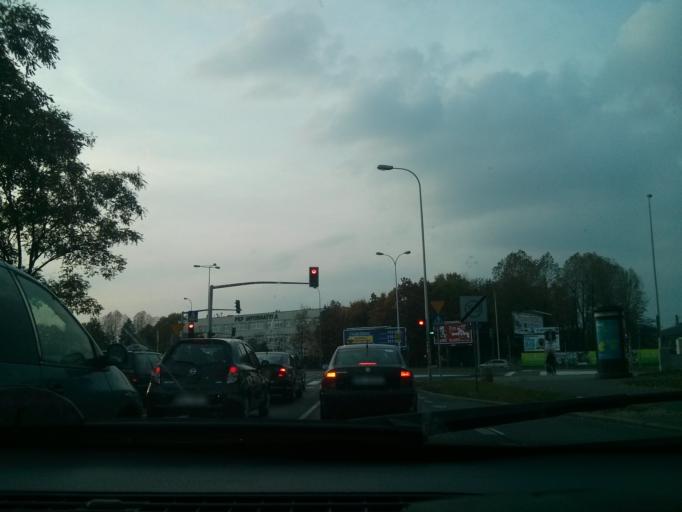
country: PL
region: Masovian Voivodeship
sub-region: Warszawa
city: Ochota
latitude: 52.2195
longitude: 20.9720
